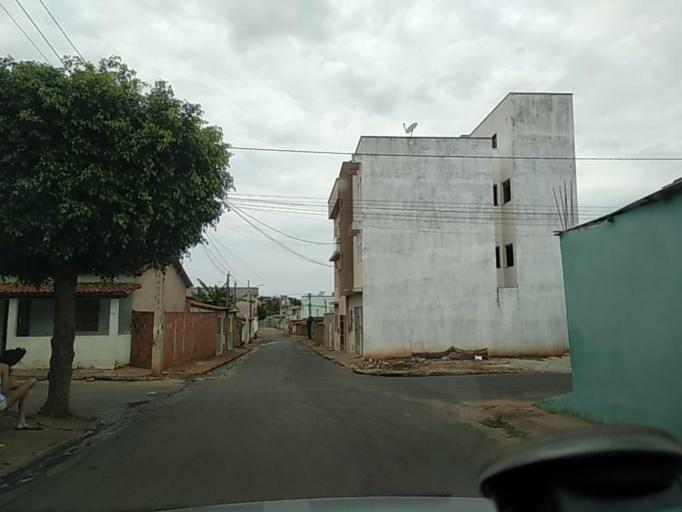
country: BR
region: Bahia
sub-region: Caetite
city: Caetite
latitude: -14.0589
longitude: -42.4809
